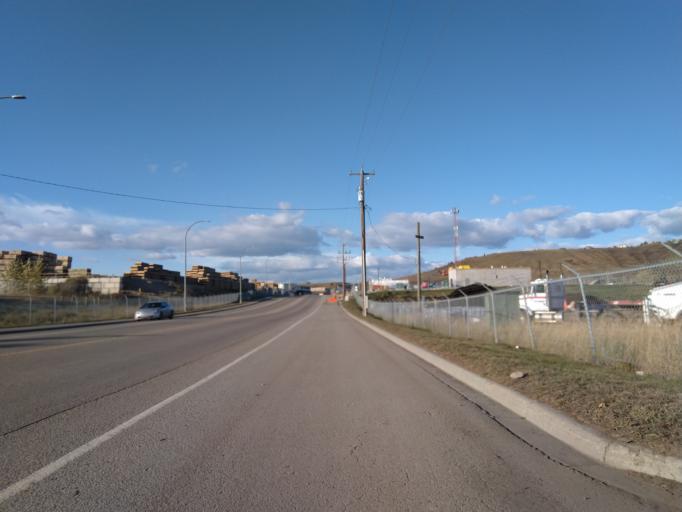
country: CA
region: Alberta
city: Cochrane
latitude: 51.1809
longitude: -114.4667
